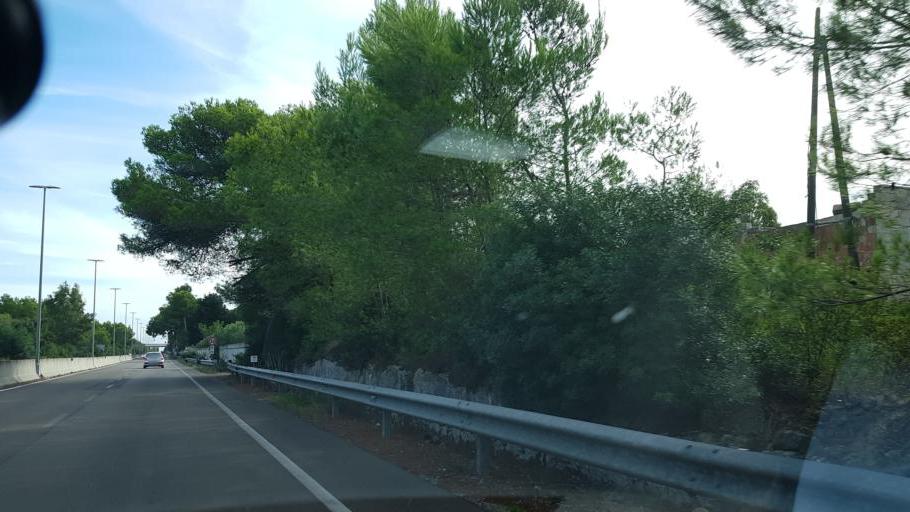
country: IT
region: Apulia
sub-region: Provincia di Lecce
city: Struda
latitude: 40.3864
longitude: 18.2926
